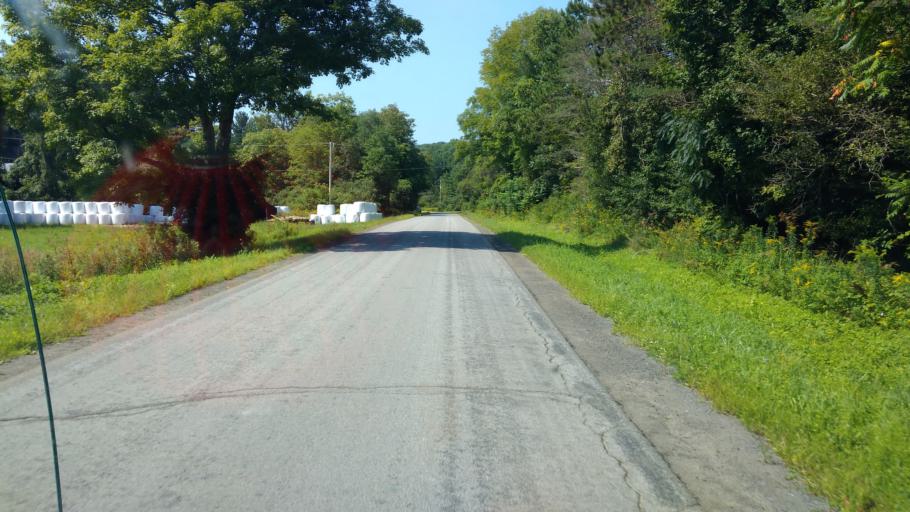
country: US
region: New York
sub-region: Allegany County
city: Belmont
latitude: 42.2525
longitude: -78.0075
